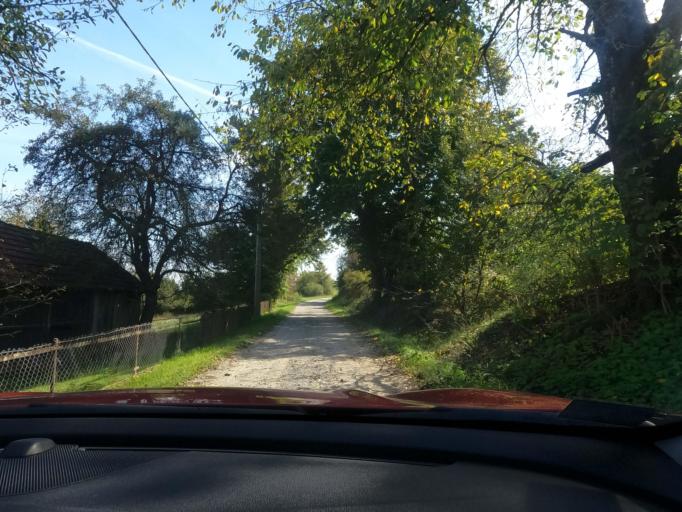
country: HR
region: Sisacko-Moslavacka
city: Petrinja
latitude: 45.3410
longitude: 16.2425
